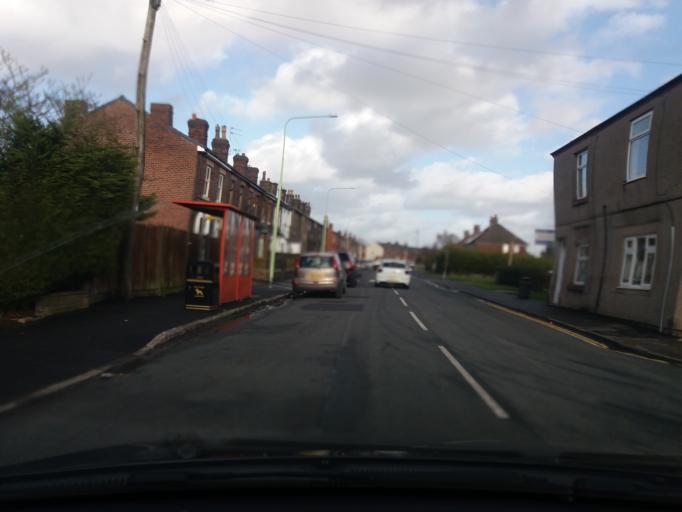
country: GB
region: England
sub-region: Lancashire
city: Adlington
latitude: 53.6103
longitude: -2.6142
